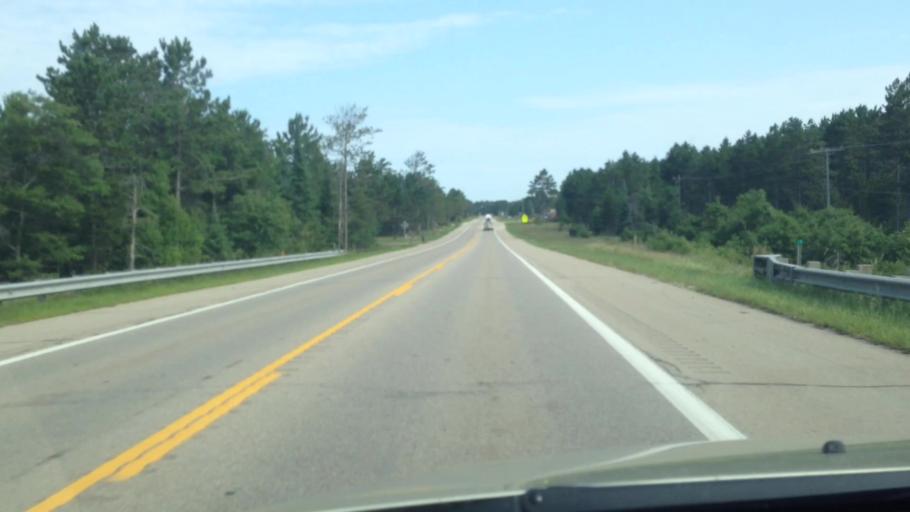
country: US
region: Michigan
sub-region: Delta County
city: Gladstone
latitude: 45.9080
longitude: -86.9297
